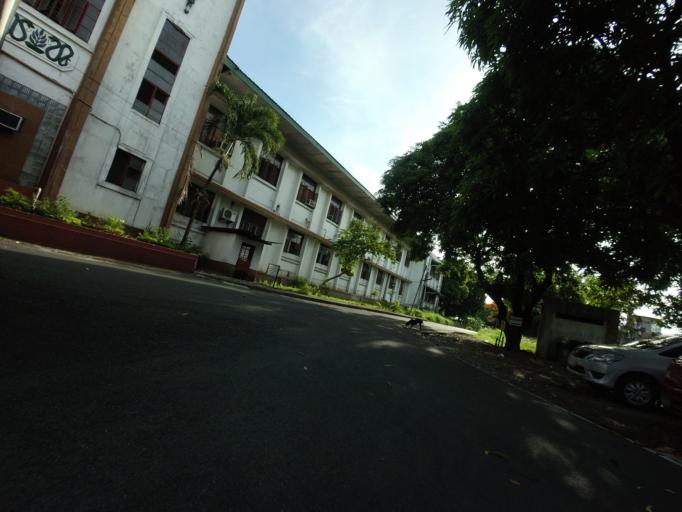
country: PH
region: Metro Manila
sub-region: Mandaluyong
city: Mandaluyong City
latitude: 14.5845
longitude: 121.0436
